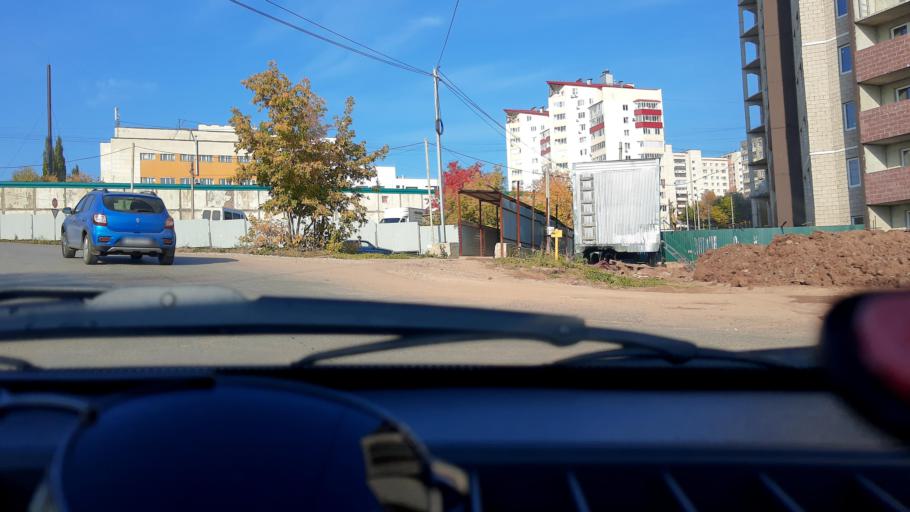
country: RU
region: Bashkortostan
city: Ufa
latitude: 54.7753
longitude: 56.0399
